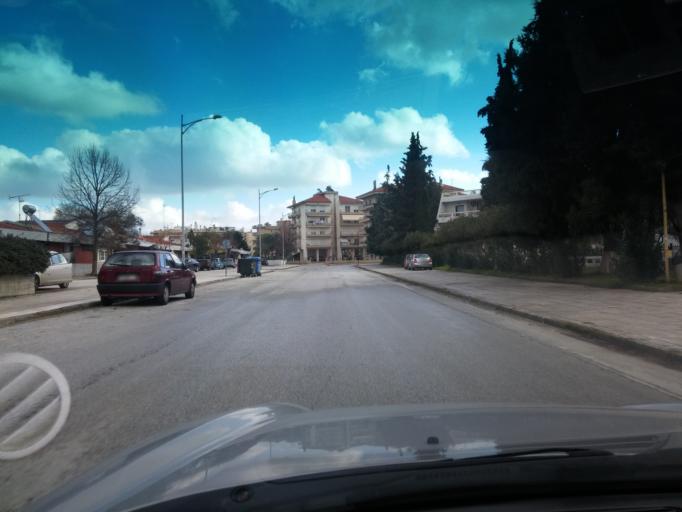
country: GR
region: East Macedonia and Thrace
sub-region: Nomos Rodopis
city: Komotini
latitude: 41.1217
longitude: 25.3906
